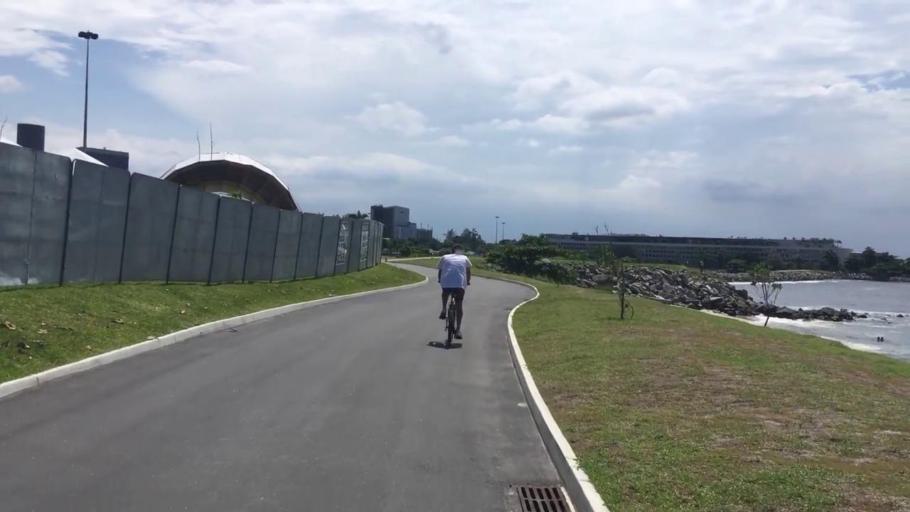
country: BR
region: Rio de Janeiro
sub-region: Rio De Janeiro
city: Rio de Janeiro
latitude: -22.9203
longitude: -43.1680
